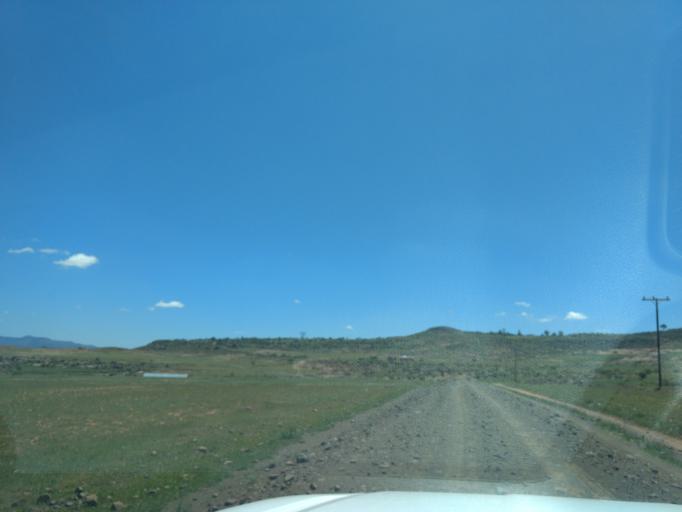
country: LS
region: Maseru
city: Maseru
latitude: -29.4686
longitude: 27.3757
